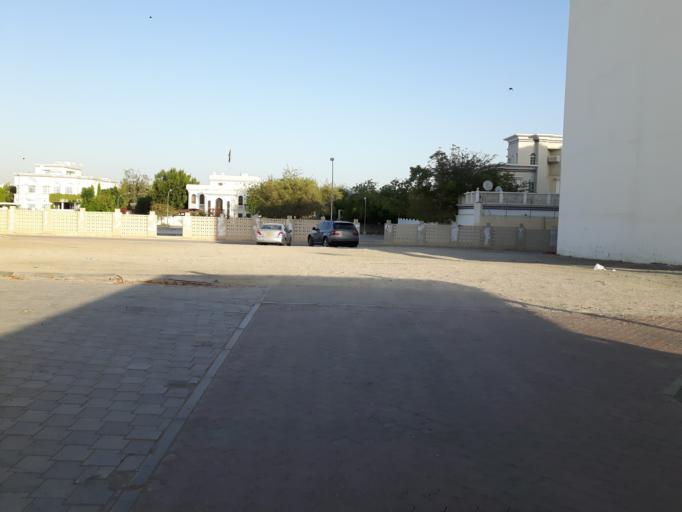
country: OM
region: Muhafazat Masqat
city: Bawshar
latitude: 23.6114
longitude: 58.4533
